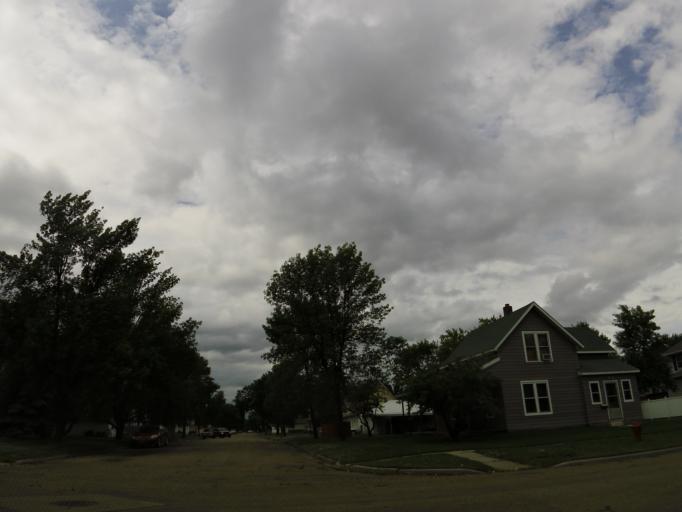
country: US
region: North Dakota
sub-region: Walsh County
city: Grafton
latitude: 48.4145
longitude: -97.4126
